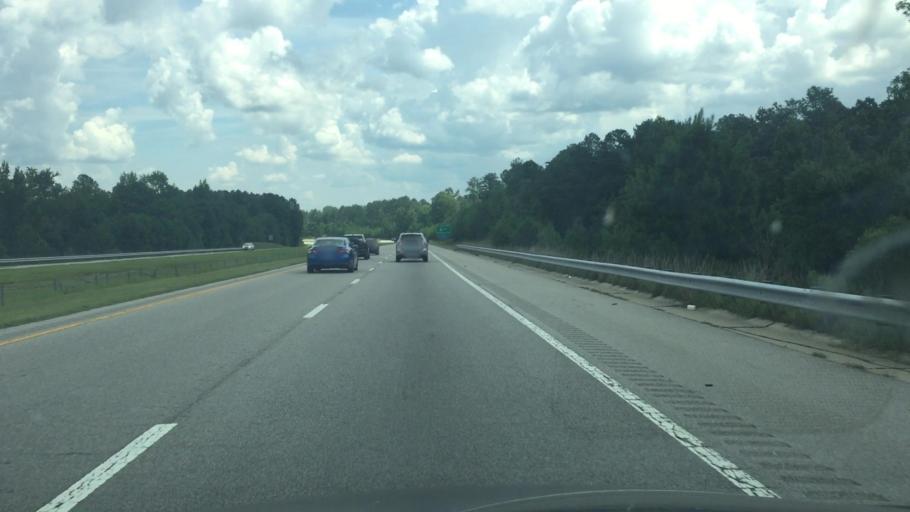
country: US
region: North Carolina
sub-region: Richmond County
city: Ellerbe
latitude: 35.0596
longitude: -79.7464
